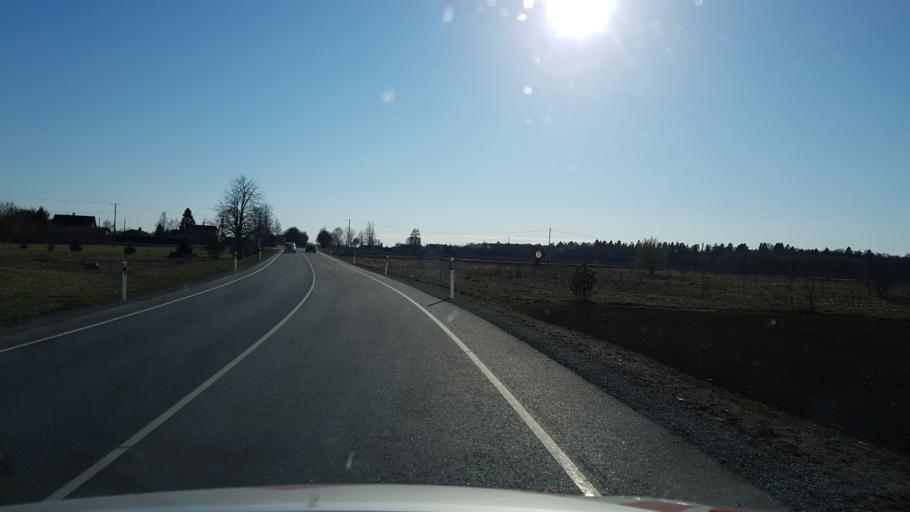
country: EE
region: Ida-Virumaa
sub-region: Johvi vald
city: Johvi
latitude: 59.3515
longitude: 27.3828
